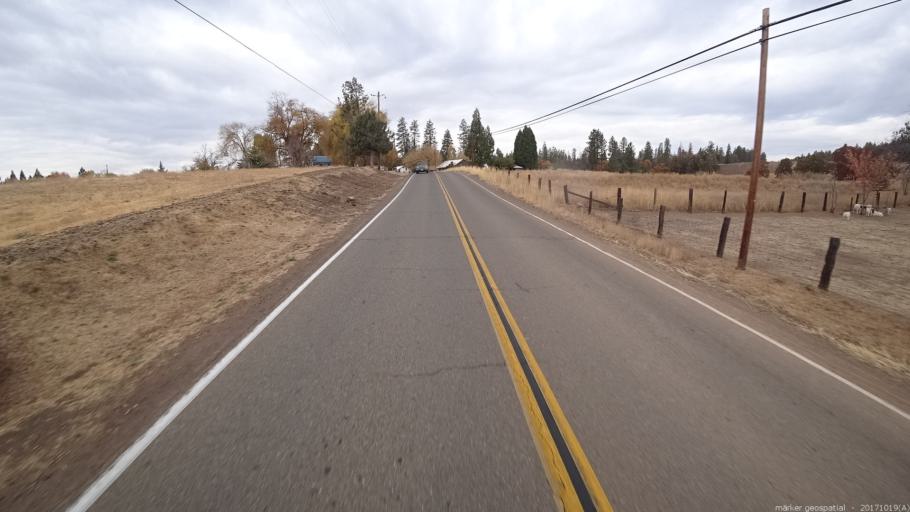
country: US
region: California
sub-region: Shasta County
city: Burney
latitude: 41.0491
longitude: -121.3351
